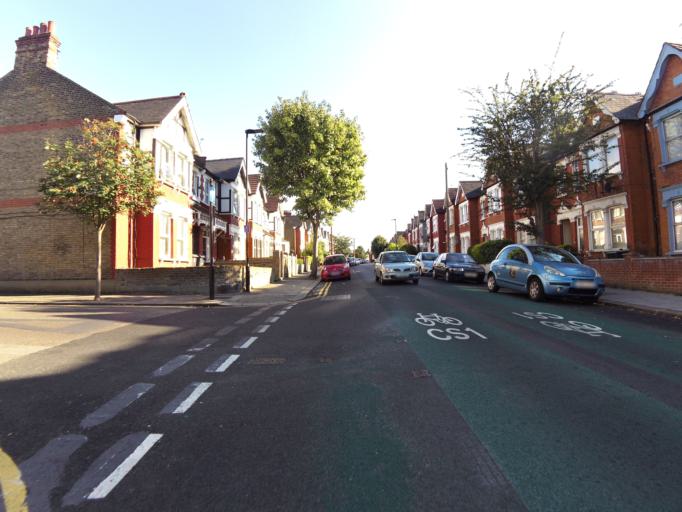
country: GB
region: England
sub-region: Greater London
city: Harringay
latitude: 51.5965
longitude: -0.0757
